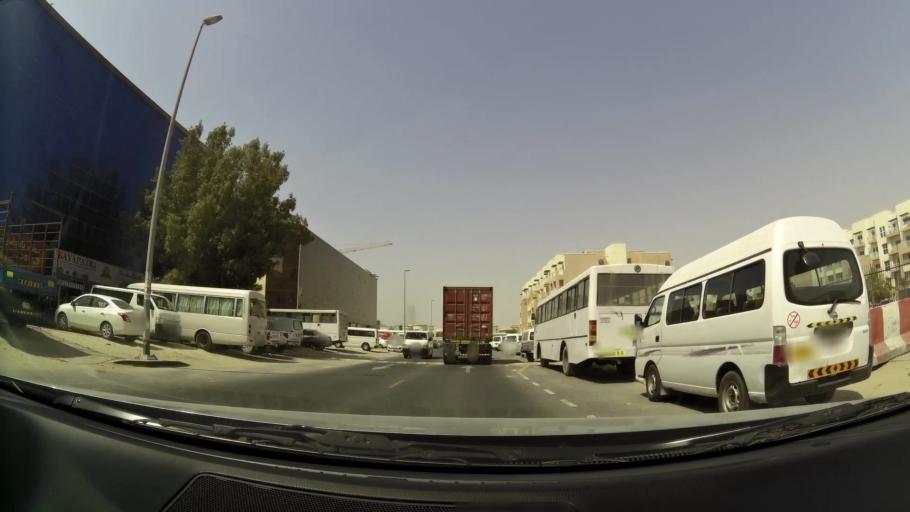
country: AE
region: Dubai
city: Dubai
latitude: 25.1581
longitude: 55.2513
